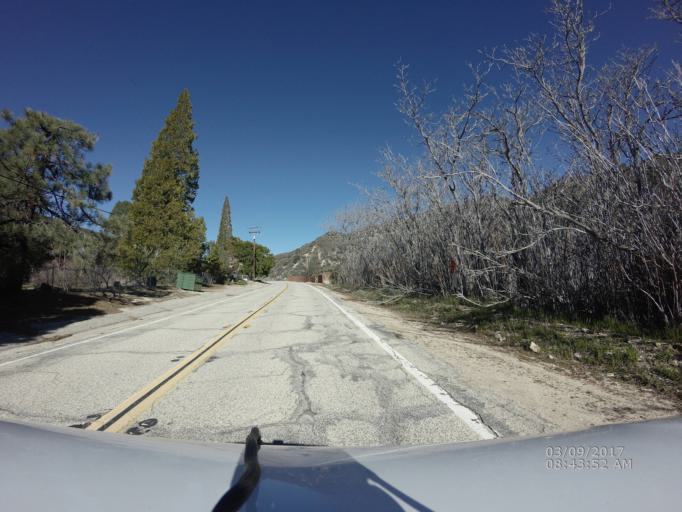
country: US
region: California
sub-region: Los Angeles County
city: Green Valley
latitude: 34.6938
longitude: -118.4930
